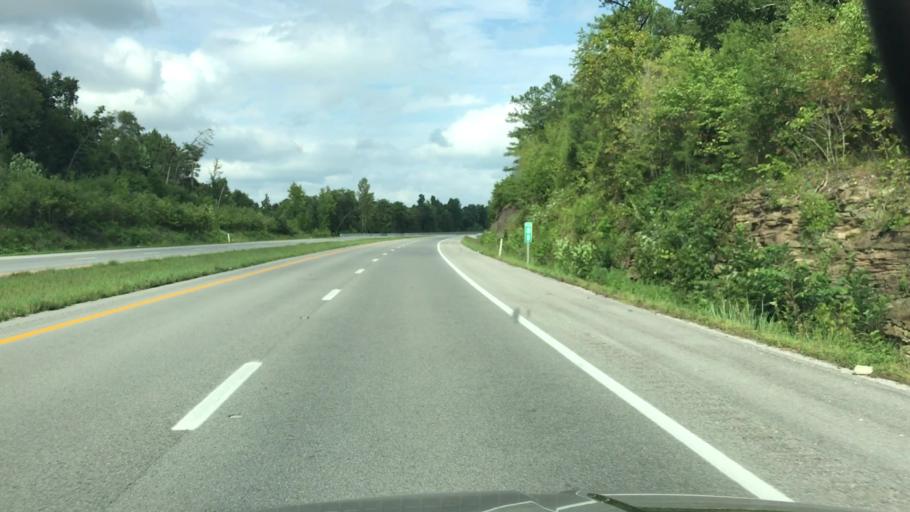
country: US
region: Kentucky
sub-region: Hopkins County
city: Dawson Springs
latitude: 37.1636
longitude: -87.7587
